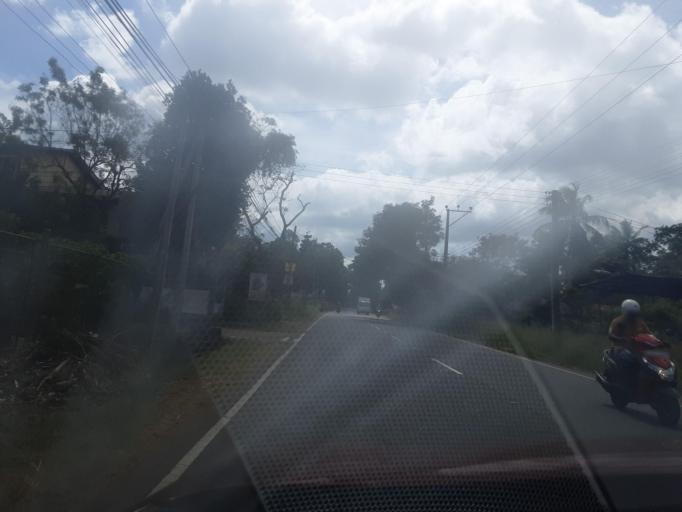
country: LK
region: North Western
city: Kuliyapitiya
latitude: 7.4810
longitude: 79.9947
